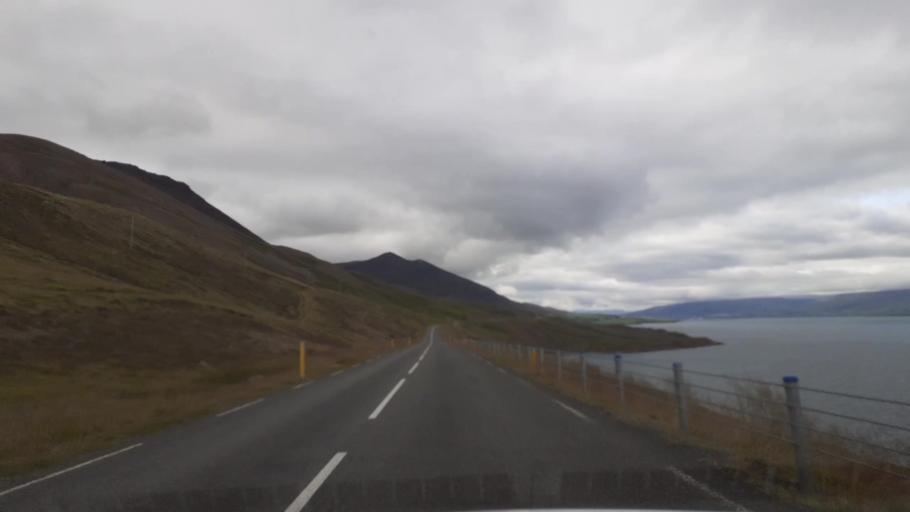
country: IS
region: Northeast
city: Akureyri
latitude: 65.8474
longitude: -18.0591
